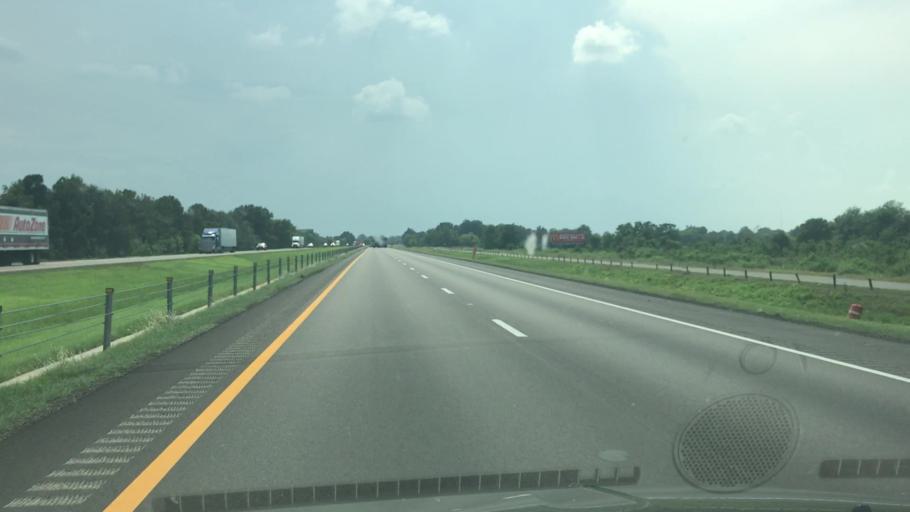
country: US
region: Arkansas
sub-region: Crittenden County
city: Earle
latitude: 35.1396
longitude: -90.4267
